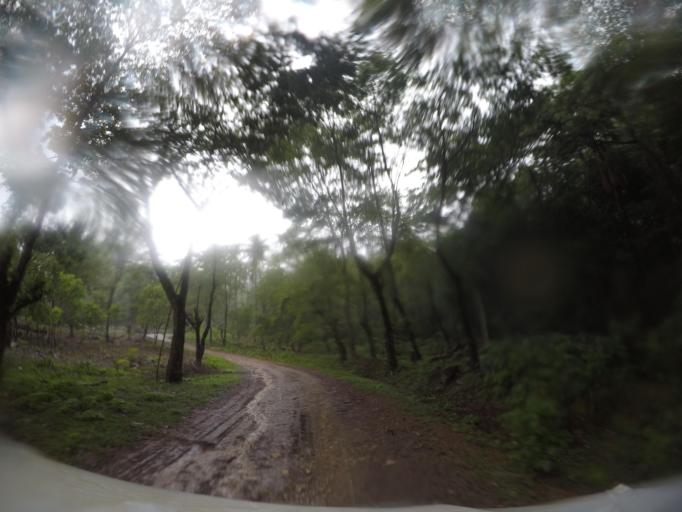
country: TL
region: Baucau
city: Venilale
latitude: -8.6295
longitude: 126.4355
